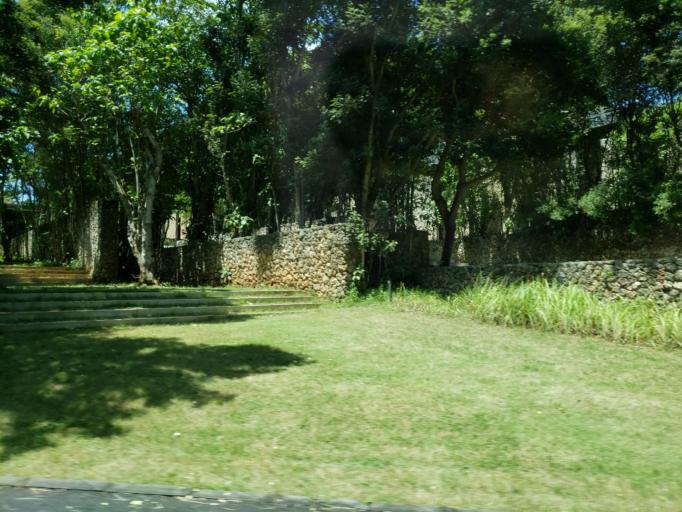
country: ID
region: Bali
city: Kangin
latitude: -8.8446
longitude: 115.1379
